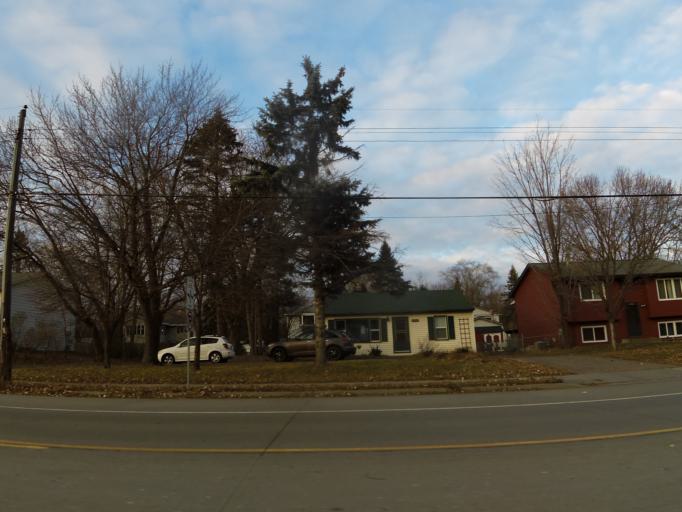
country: US
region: Minnesota
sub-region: Ramsey County
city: White Bear Lake
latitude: 45.0792
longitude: -93.0249
